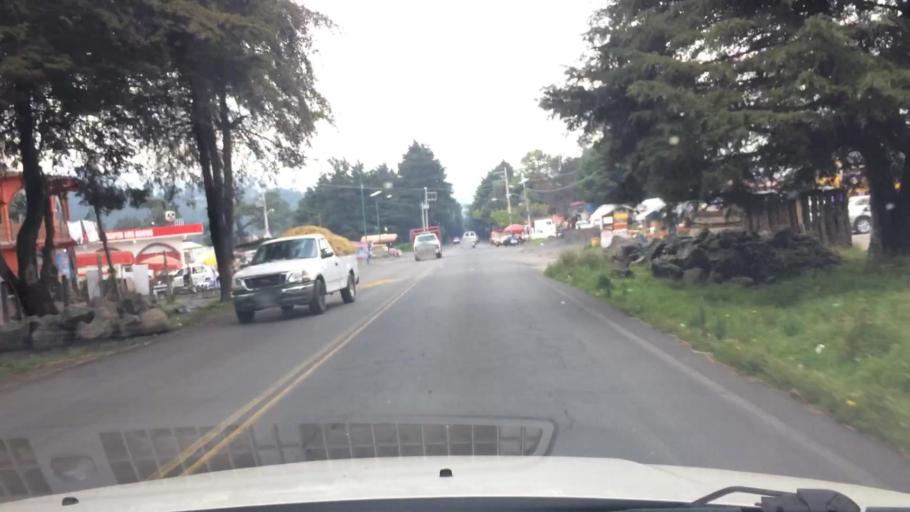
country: MX
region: Mexico City
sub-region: Tlalpan
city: Lomas de Tepemecatl
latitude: 19.2375
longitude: -99.2349
